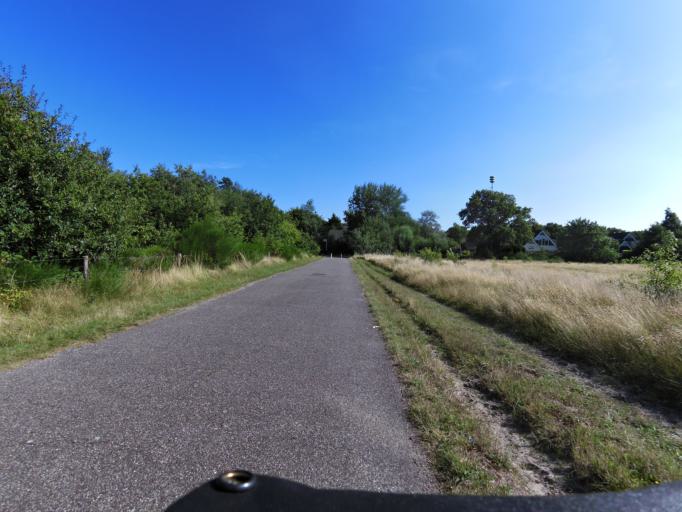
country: NL
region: Zeeland
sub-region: Schouwen-Duiveland
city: Haamstede
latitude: 51.7114
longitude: 3.7328
